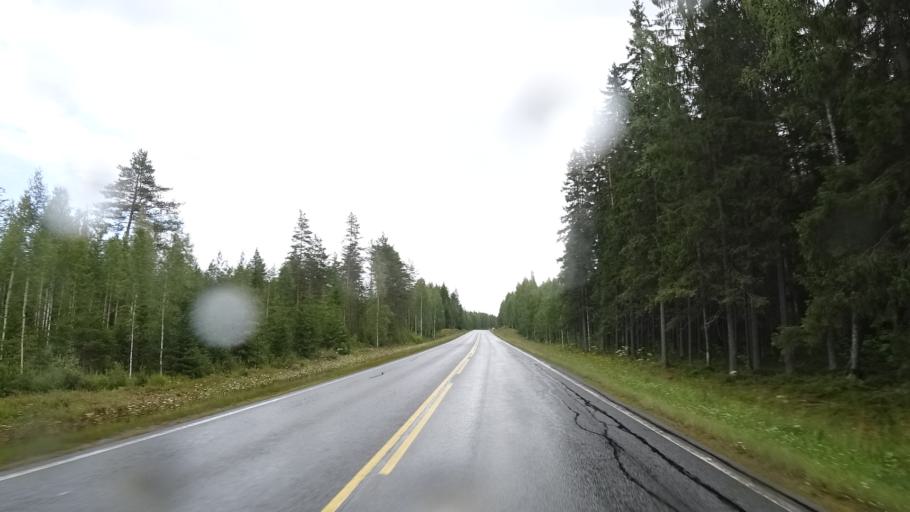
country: FI
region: North Karelia
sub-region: Keski-Karjala
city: Kesaelahti
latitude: 62.1073
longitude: 29.7925
